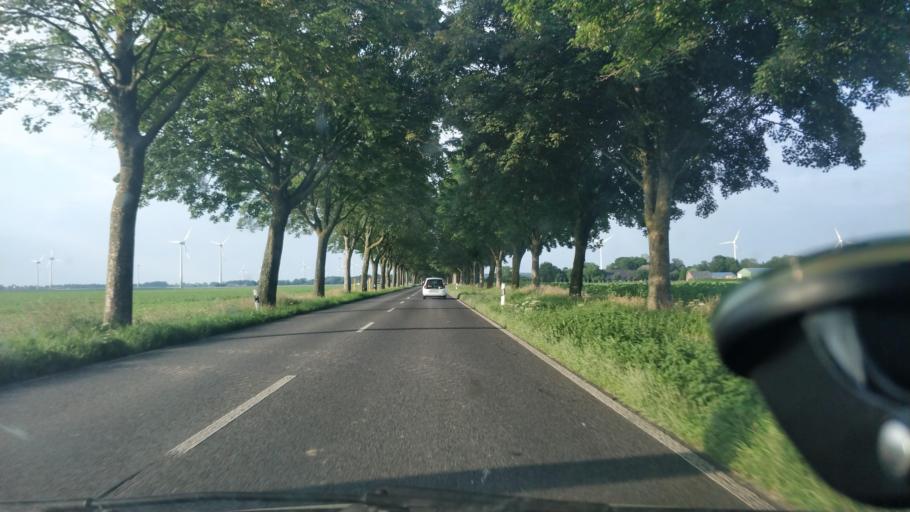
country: DE
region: North Rhine-Westphalia
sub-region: Regierungsbezirk Dusseldorf
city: Rheurdt
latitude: 51.4493
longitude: 6.4248
